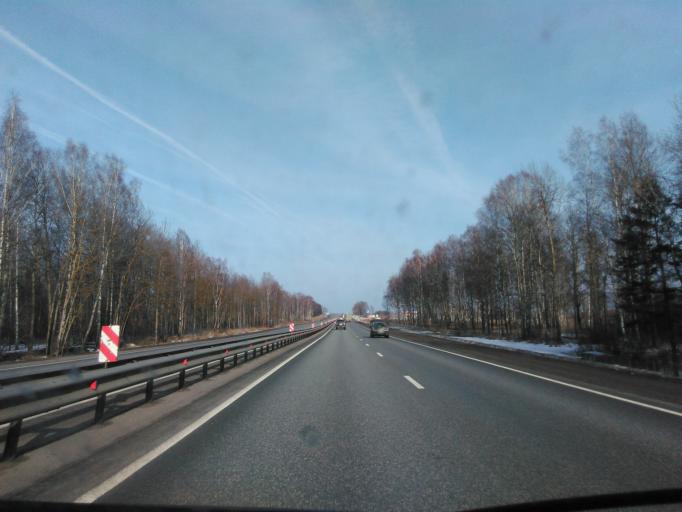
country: RU
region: Smolensk
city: Verkhnedneprovskiy
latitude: 55.1760
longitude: 33.4451
